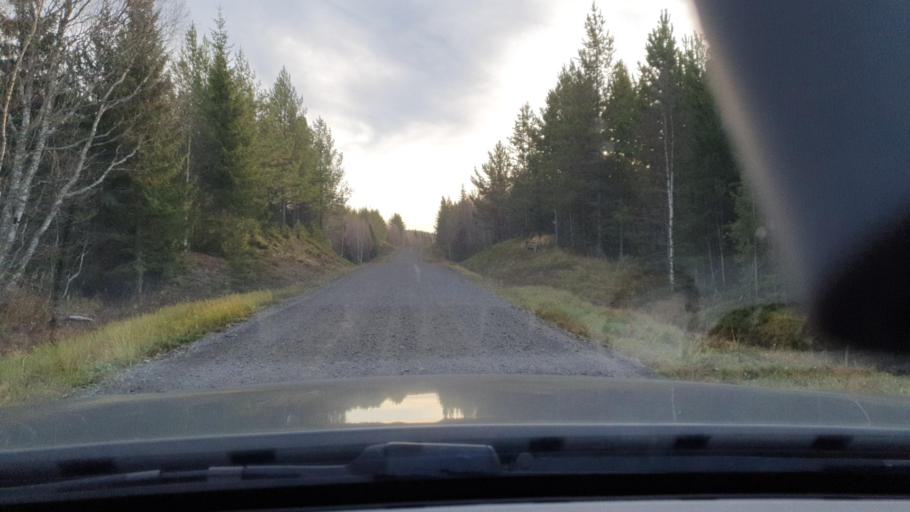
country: SE
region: Jaemtland
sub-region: Stroemsunds Kommun
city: Stroemsund
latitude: 63.5410
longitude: 15.5820
